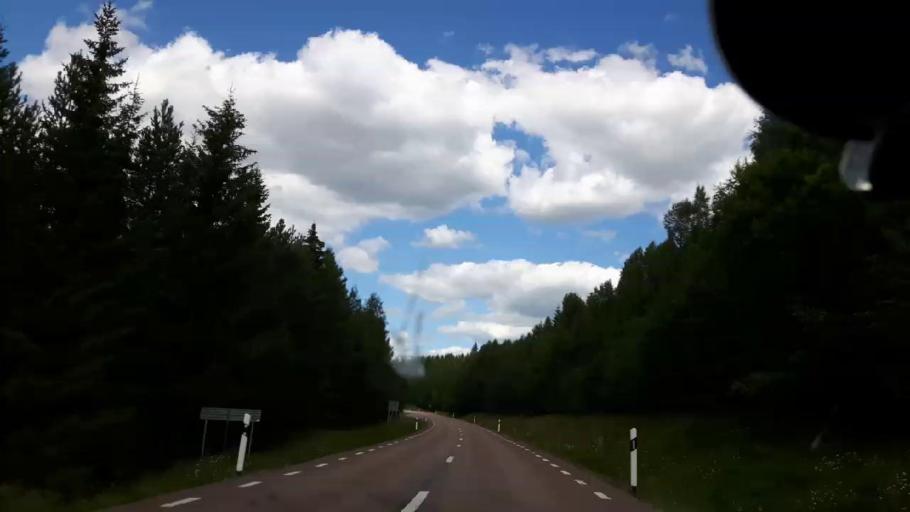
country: SE
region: Jaemtland
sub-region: Ragunda Kommun
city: Hammarstrand
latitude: 62.9182
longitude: 16.7040
